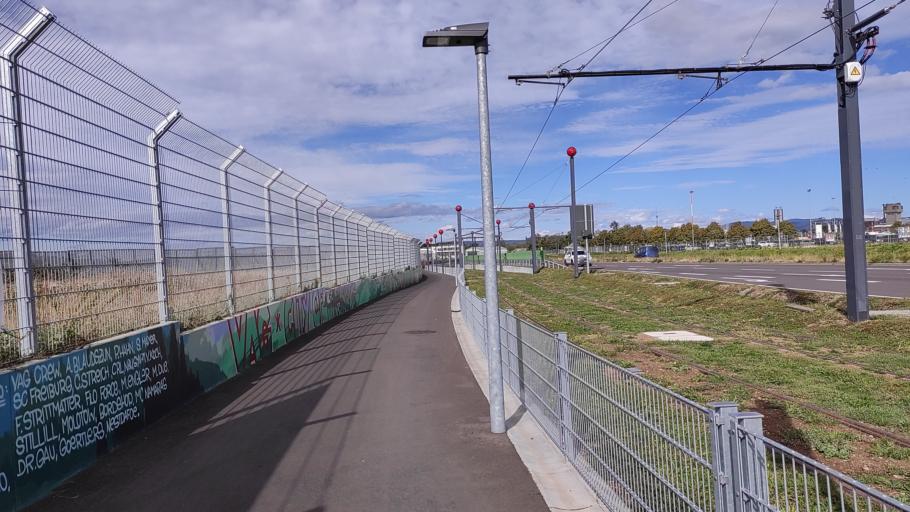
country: DE
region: Baden-Wuerttemberg
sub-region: Freiburg Region
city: Freiburg
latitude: 48.0157
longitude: 7.8365
